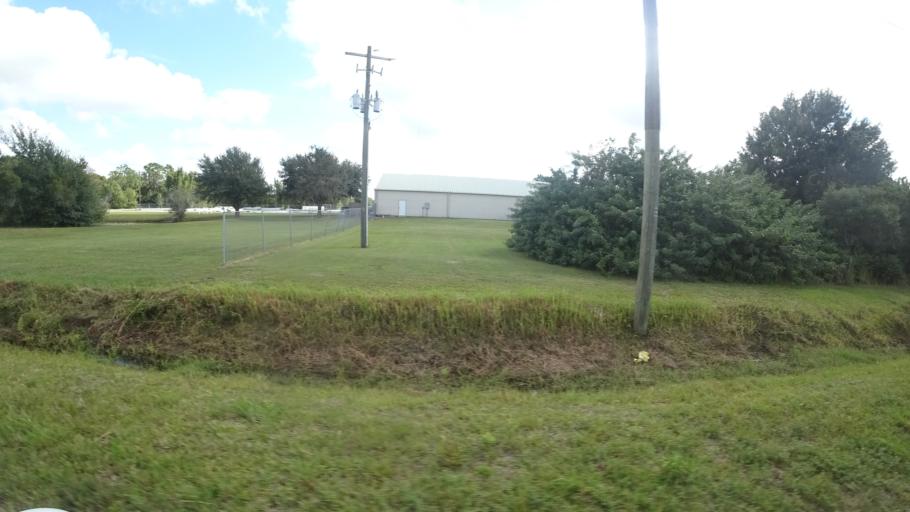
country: US
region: Florida
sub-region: Sarasota County
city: Fruitville
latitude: 27.4077
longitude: -82.2710
